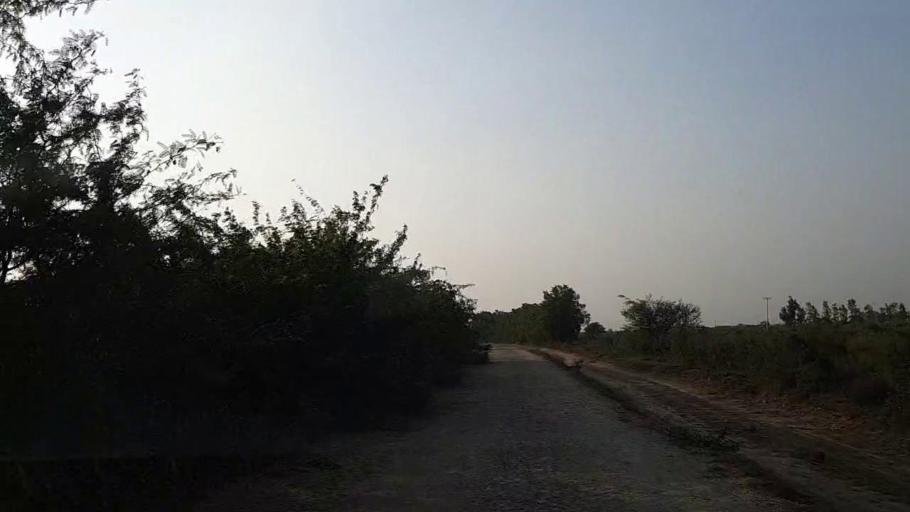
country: PK
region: Sindh
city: Thatta
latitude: 24.6923
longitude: 67.7897
